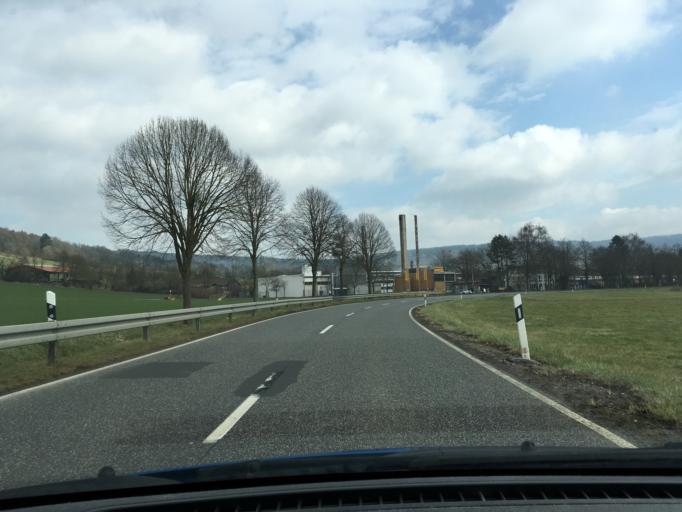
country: DE
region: Lower Saxony
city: Bodenfelde
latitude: 51.5965
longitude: 9.5870
